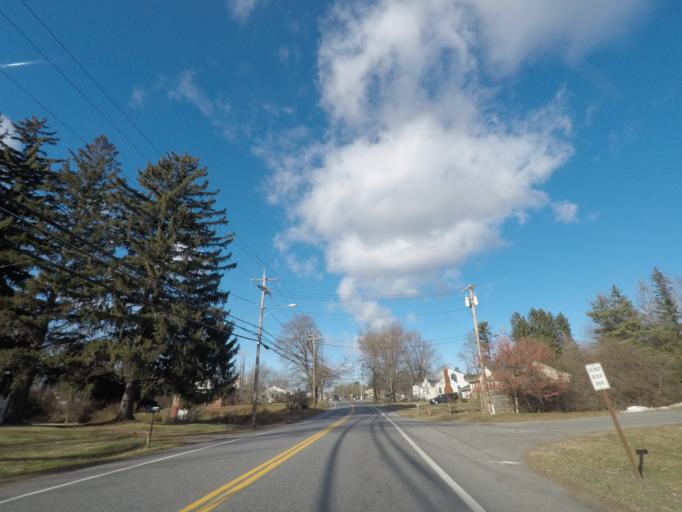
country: US
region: New York
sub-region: Saratoga County
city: Waterford
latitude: 42.8367
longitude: -73.7365
